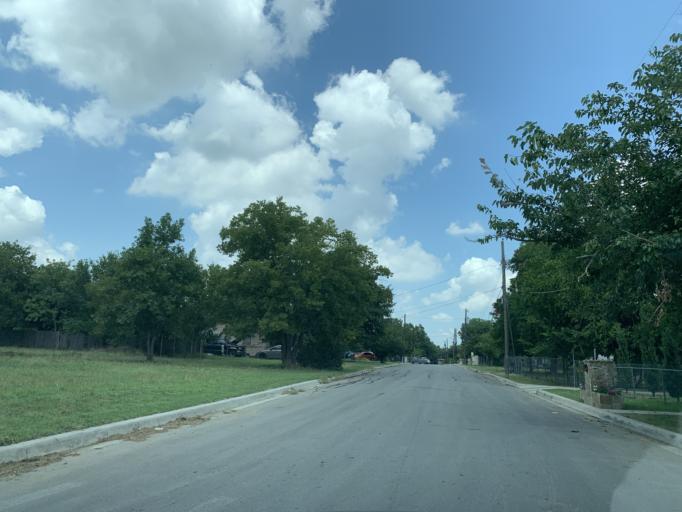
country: US
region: Texas
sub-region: Tarrant County
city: Forest Hill
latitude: 32.7323
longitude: -97.2435
